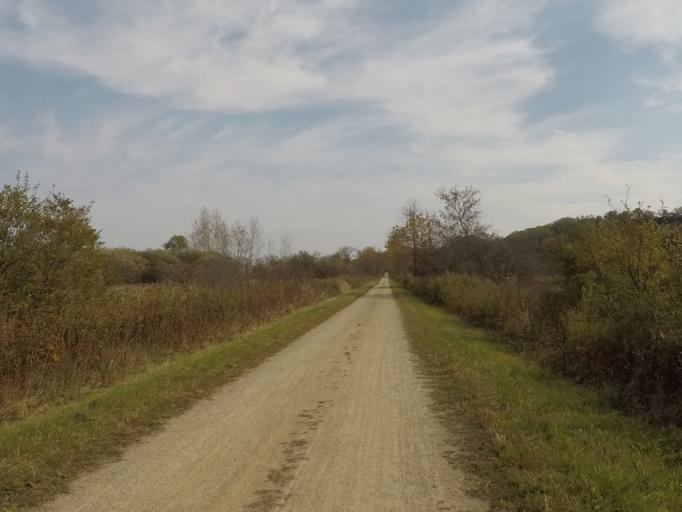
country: US
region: Wisconsin
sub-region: Dane County
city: Mount Horeb
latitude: 43.0261
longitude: -89.6642
